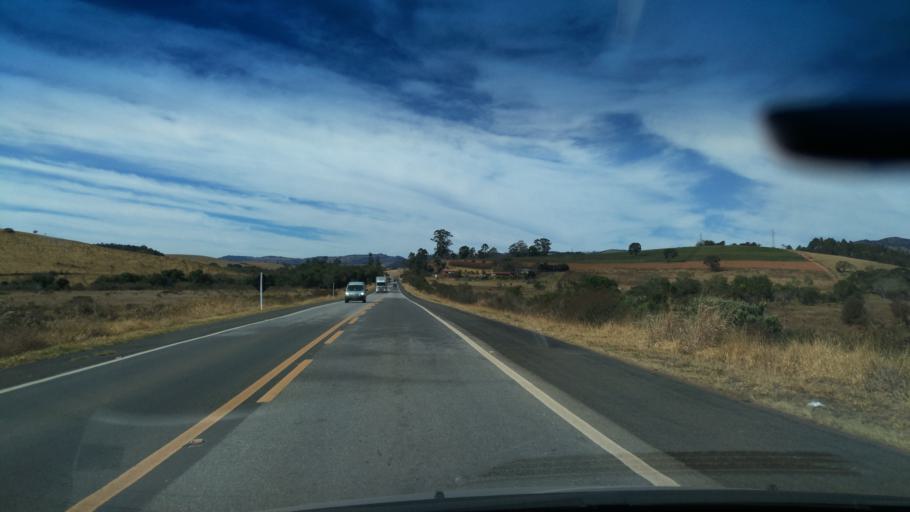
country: BR
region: Minas Gerais
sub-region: Borda Da Mata
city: Borda da Mata
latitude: -22.0563
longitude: -46.2867
